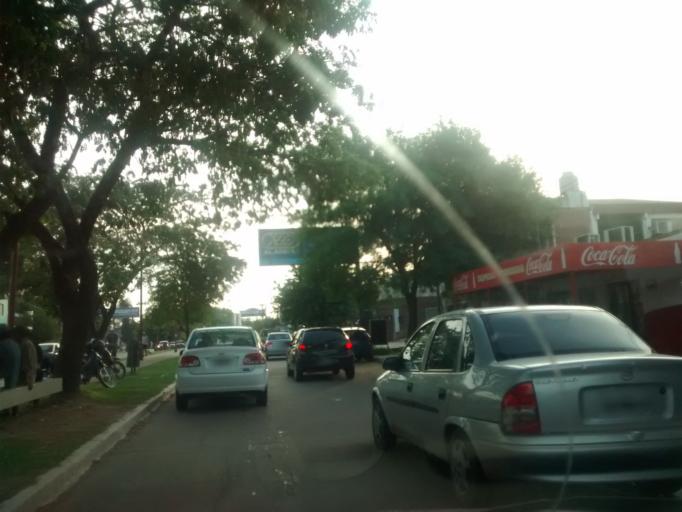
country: AR
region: Chaco
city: Resistencia
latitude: -27.4369
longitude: -58.9707
